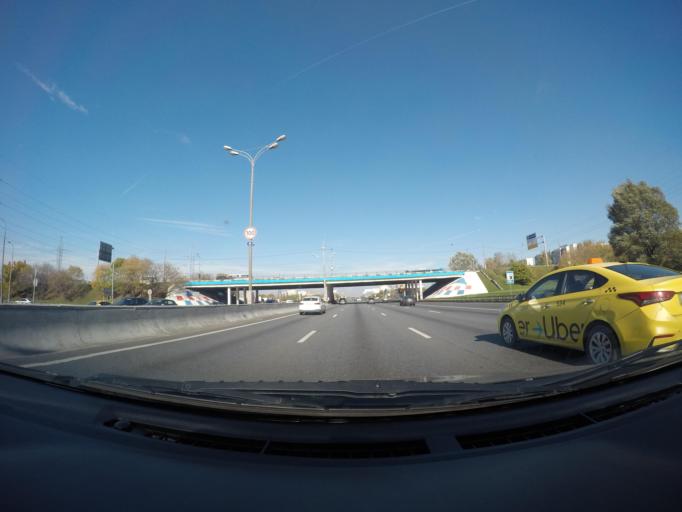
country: RU
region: Moskovskaya
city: Kuskovo
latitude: 55.7432
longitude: 37.8419
